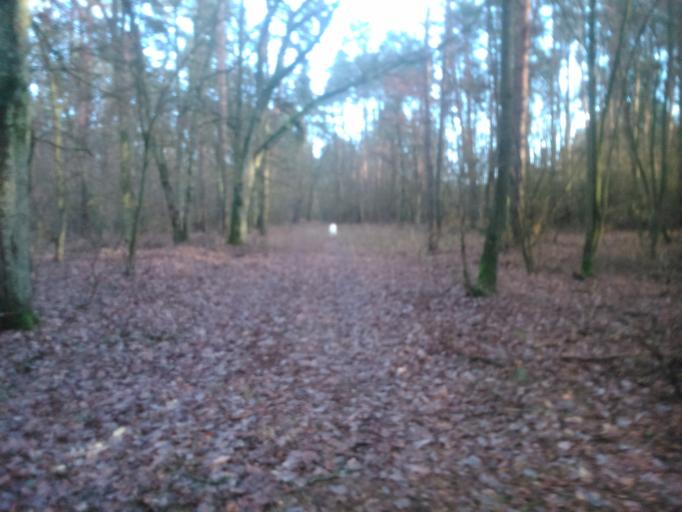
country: PL
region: Kujawsko-Pomorskie
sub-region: Powiat golubsko-dobrzynski
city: Golub-Dobrzyn
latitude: 53.1360
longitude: 19.1295
